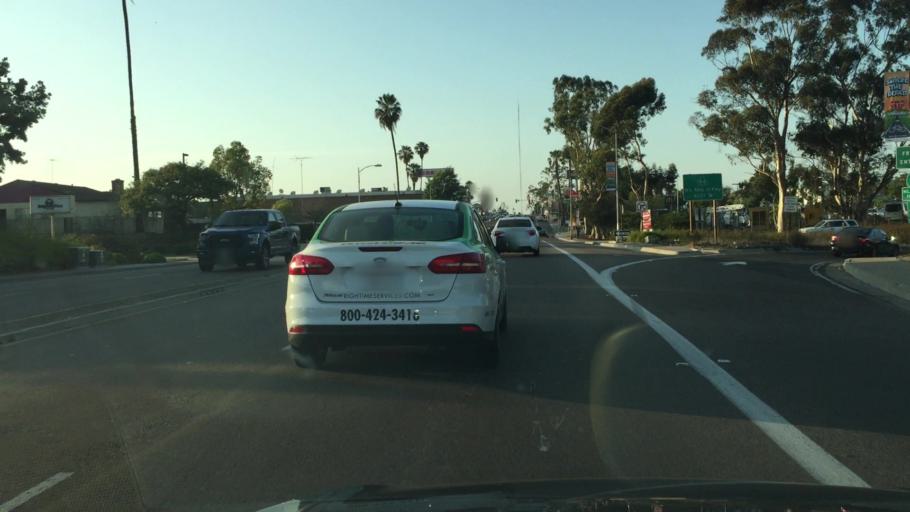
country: US
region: California
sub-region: San Diego County
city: National City
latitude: 32.7186
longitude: -117.0849
